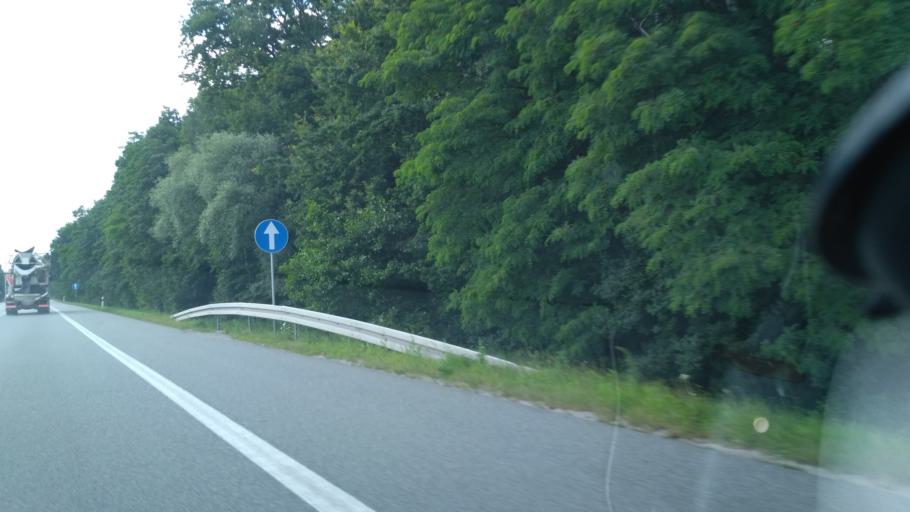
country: PL
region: Subcarpathian Voivodeship
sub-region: Powiat rzeszowski
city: Rudna Mala
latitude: 50.1205
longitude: 21.9709
